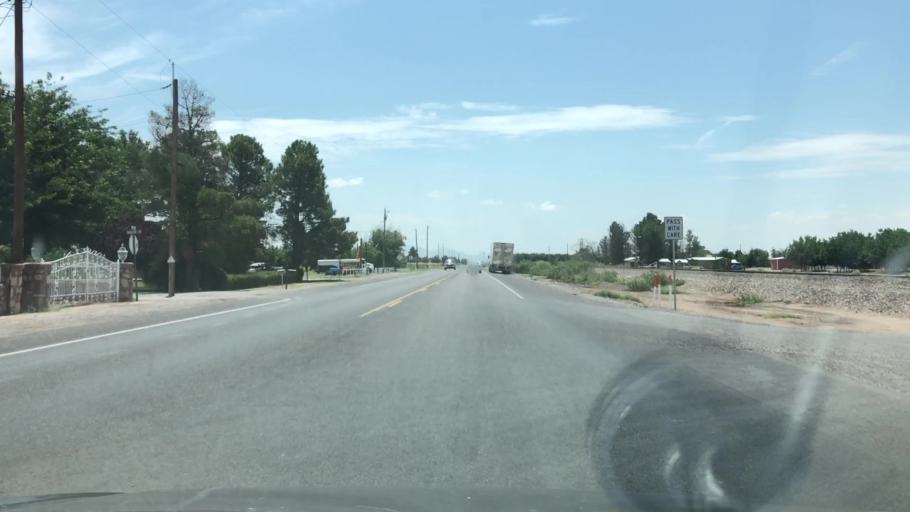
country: US
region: New Mexico
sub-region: Dona Ana County
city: Mesquite
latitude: 32.1799
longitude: -106.7063
